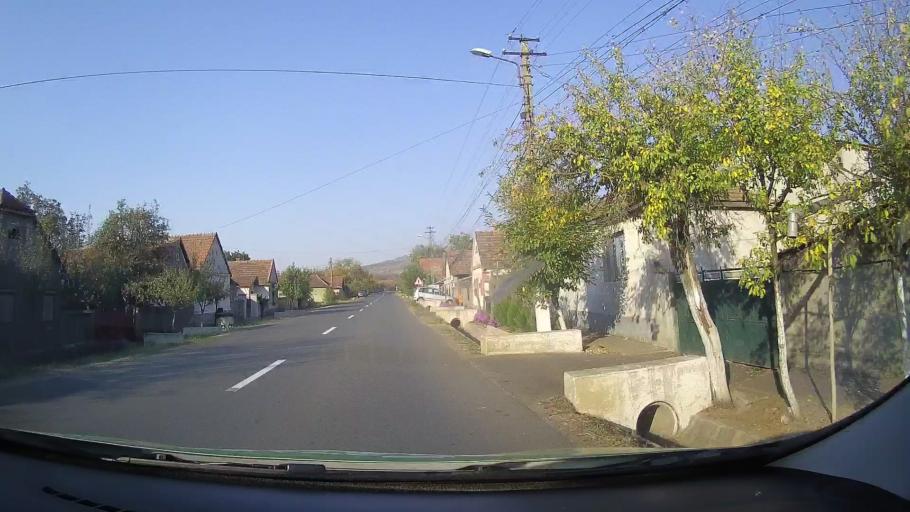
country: RO
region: Arad
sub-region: Comuna Paulis
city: Paulis
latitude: 46.1328
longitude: 21.6025
